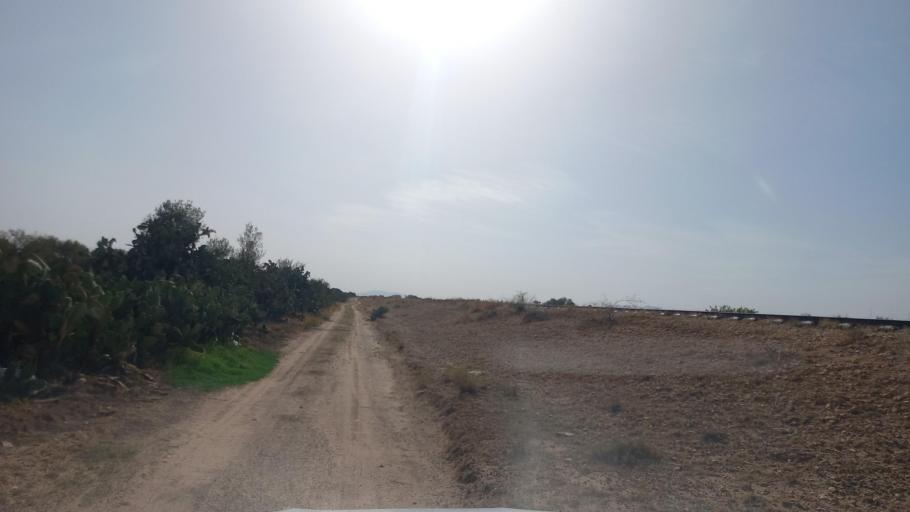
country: TN
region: Al Qasrayn
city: Kasserine
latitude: 35.2167
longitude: 8.9480
